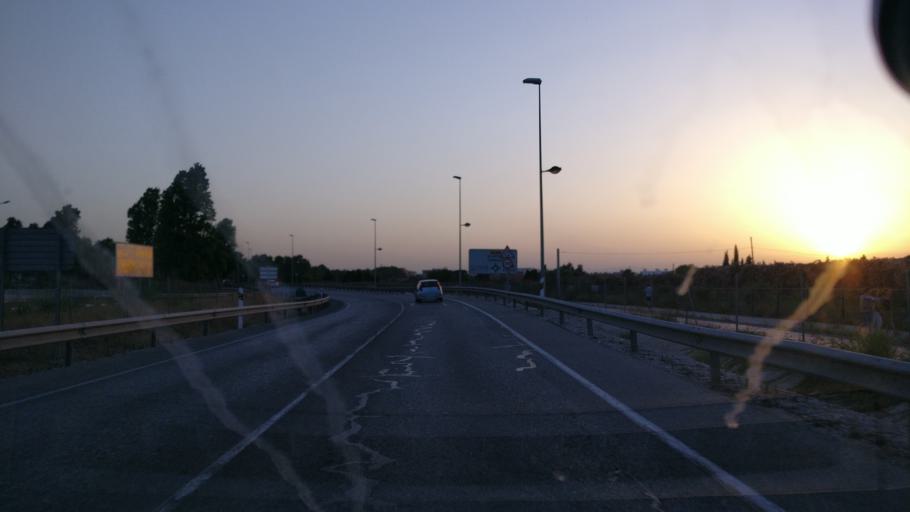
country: ES
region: Valencia
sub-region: Provincia de Valencia
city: Aldaia
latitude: 39.4648
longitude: -0.4451
